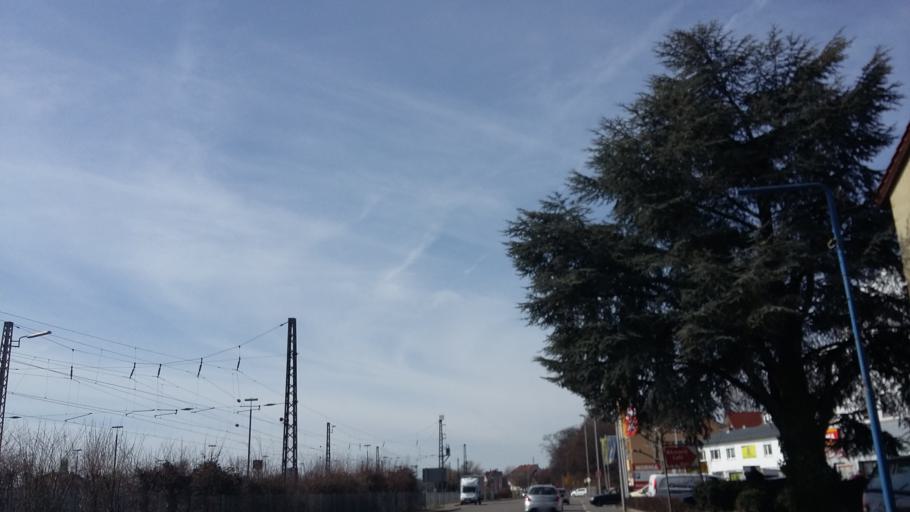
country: DE
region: Bavaria
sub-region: Swabia
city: Lindau
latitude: 47.5525
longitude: 9.7113
